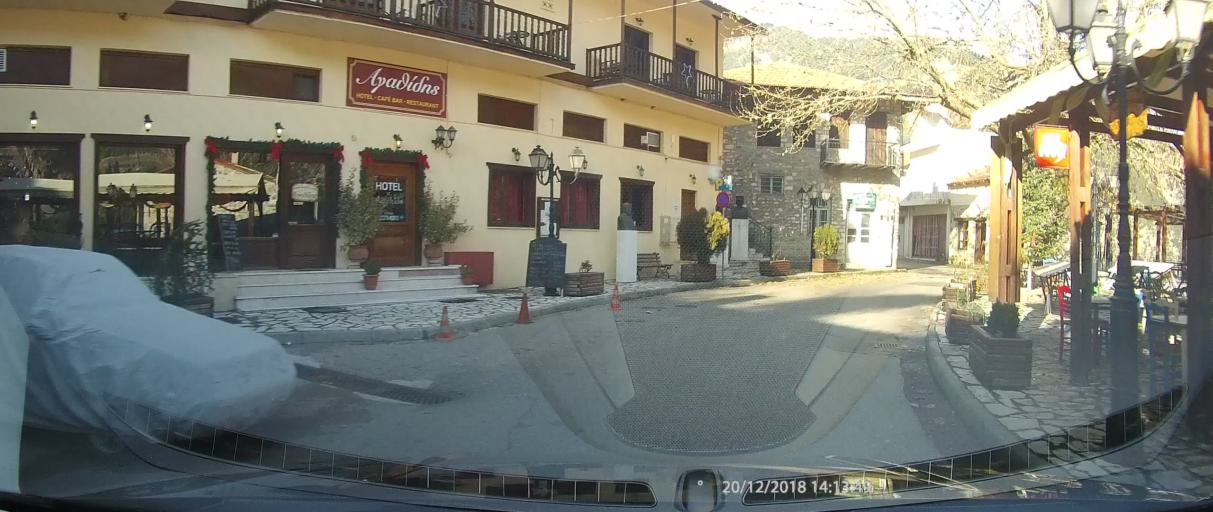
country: GR
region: West Greece
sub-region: Nomos Aitolias kai Akarnanias
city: Thermo
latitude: 38.7438
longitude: 21.6535
